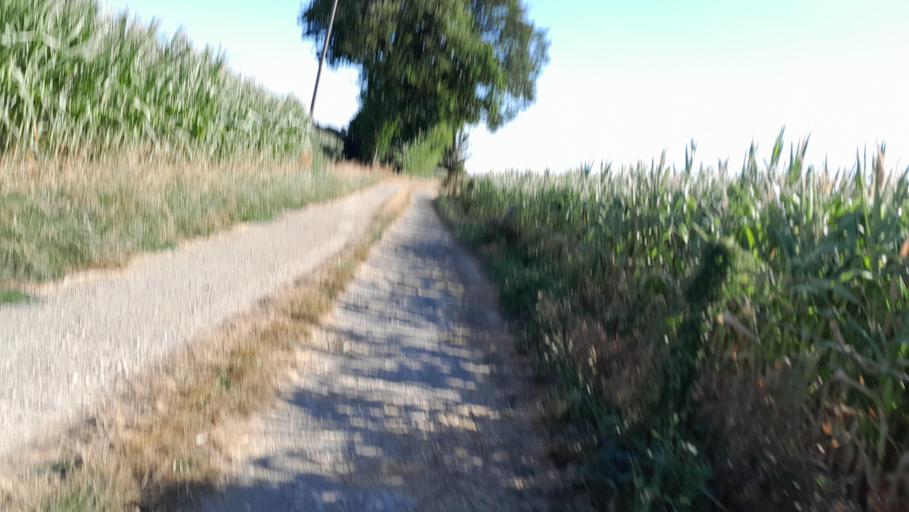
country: FR
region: Pays de la Loire
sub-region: Departement de la Mayenne
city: Ballots
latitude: 47.9639
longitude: -1.0599
